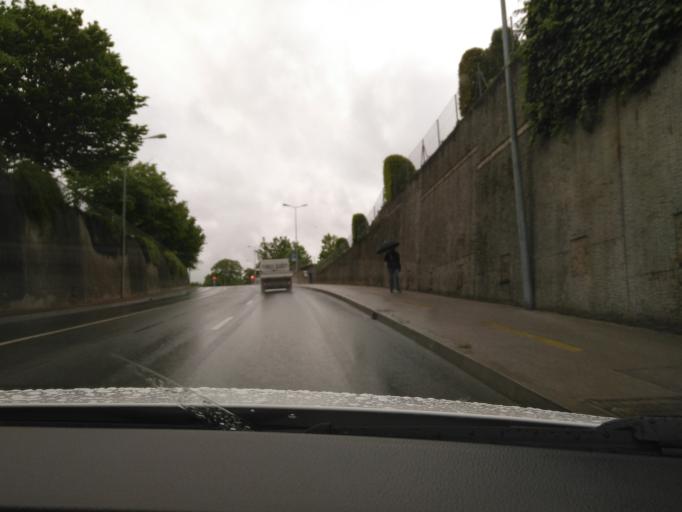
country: CH
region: Vaud
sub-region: Nyon District
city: Nyon
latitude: 46.3784
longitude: 6.2360
